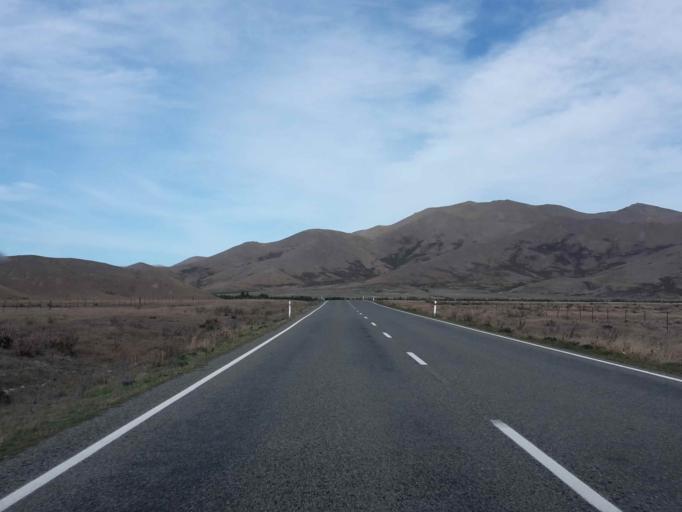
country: NZ
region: Canterbury
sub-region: Timaru District
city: Pleasant Point
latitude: -44.0904
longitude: 170.5517
